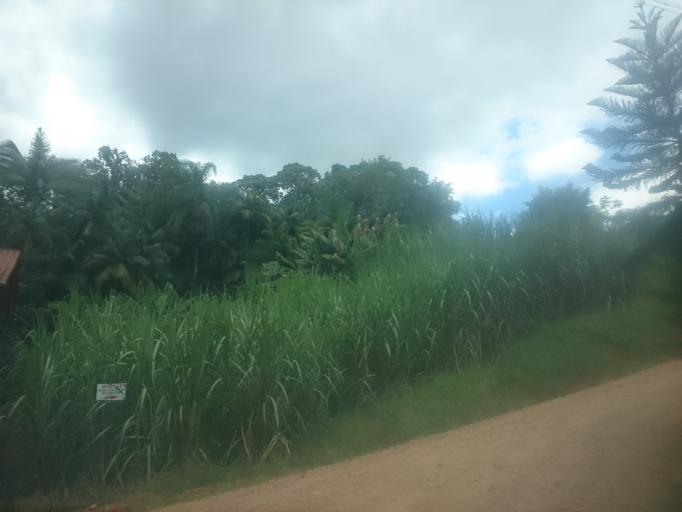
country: BR
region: Santa Catarina
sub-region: Pomerode
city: Pomerode
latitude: -26.7320
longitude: -49.1705
